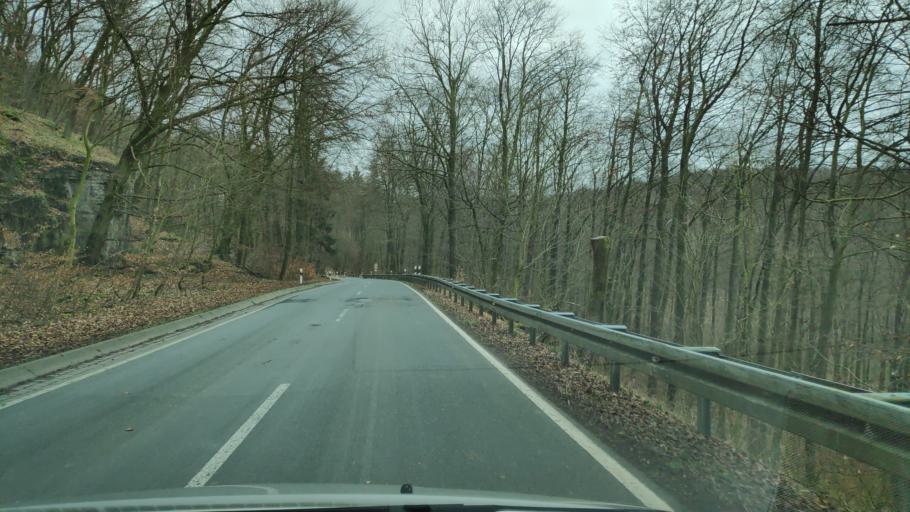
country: DE
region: Lower Saxony
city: Hessisch Oldendorf
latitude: 52.2043
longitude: 9.2786
